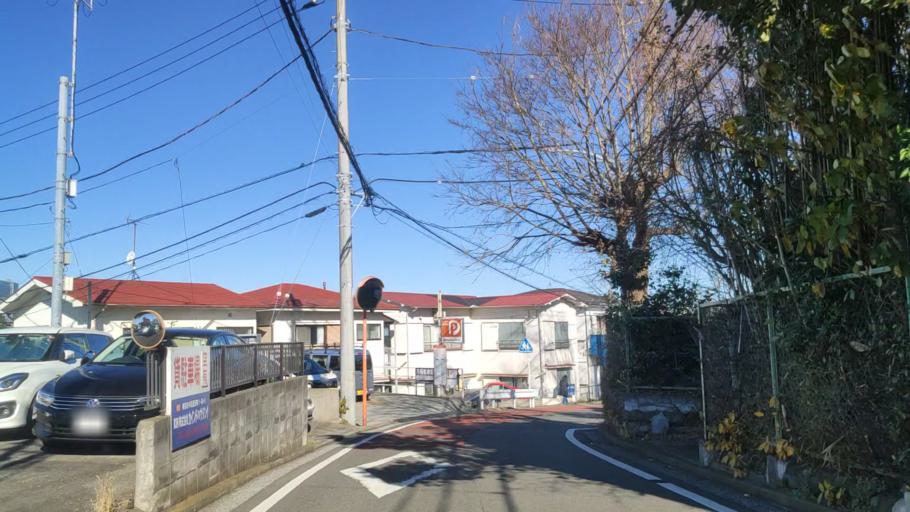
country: JP
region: Kanagawa
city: Yokohama
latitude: 35.4310
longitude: 139.6451
